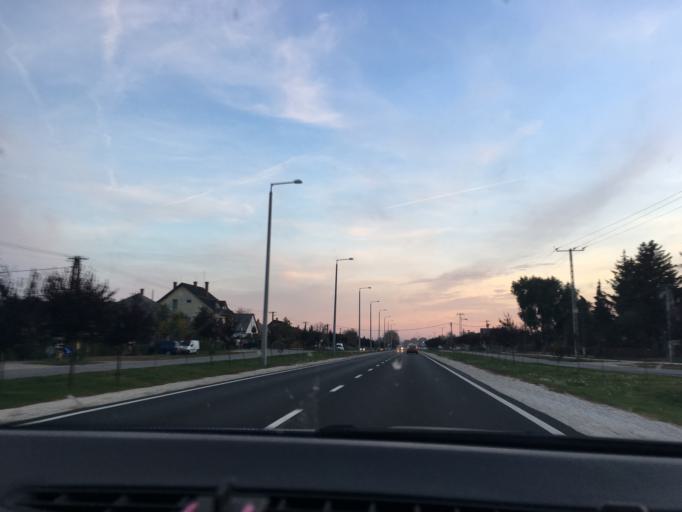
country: HU
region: Hajdu-Bihar
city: Hajduhadhaz
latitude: 47.6476
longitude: 21.6603
